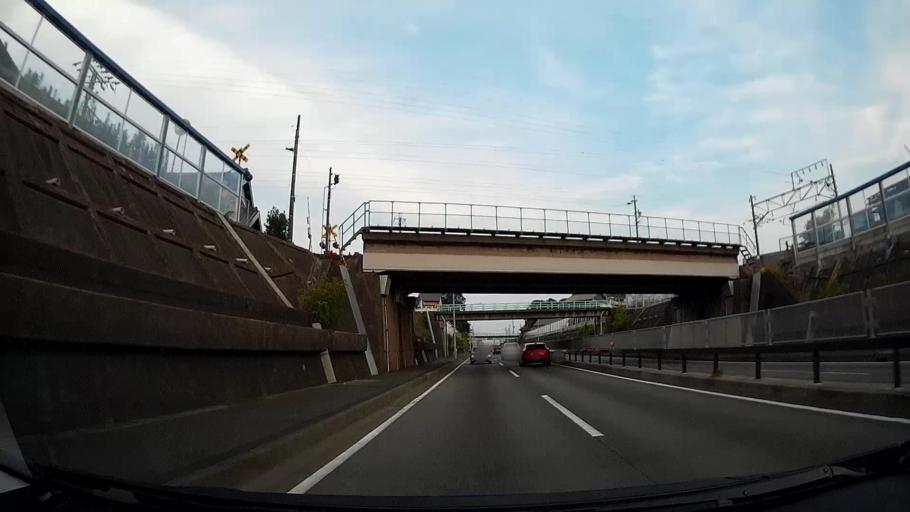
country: JP
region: Aichi
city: Kozakai-cho
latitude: 34.7999
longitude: 137.3649
